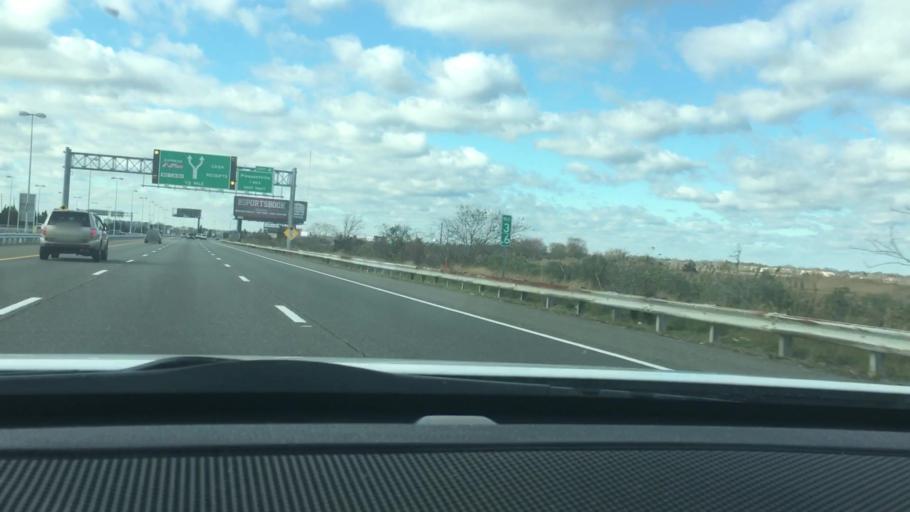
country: US
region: New Jersey
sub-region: Atlantic County
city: Pleasantville
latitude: 39.3845
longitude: -74.5005
